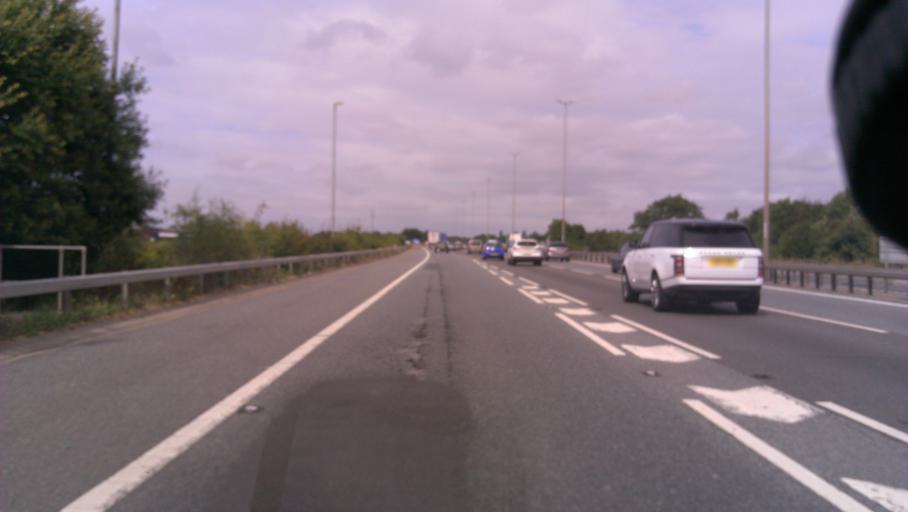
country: GB
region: England
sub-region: Essex
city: Stansted
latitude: 51.8807
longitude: 0.2040
